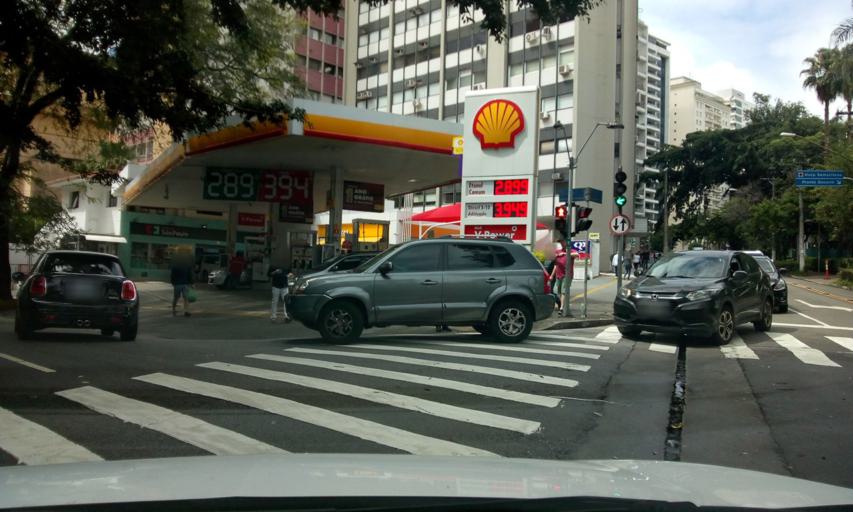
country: BR
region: Sao Paulo
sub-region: Sao Paulo
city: Sao Paulo
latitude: -23.5389
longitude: -46.6615
